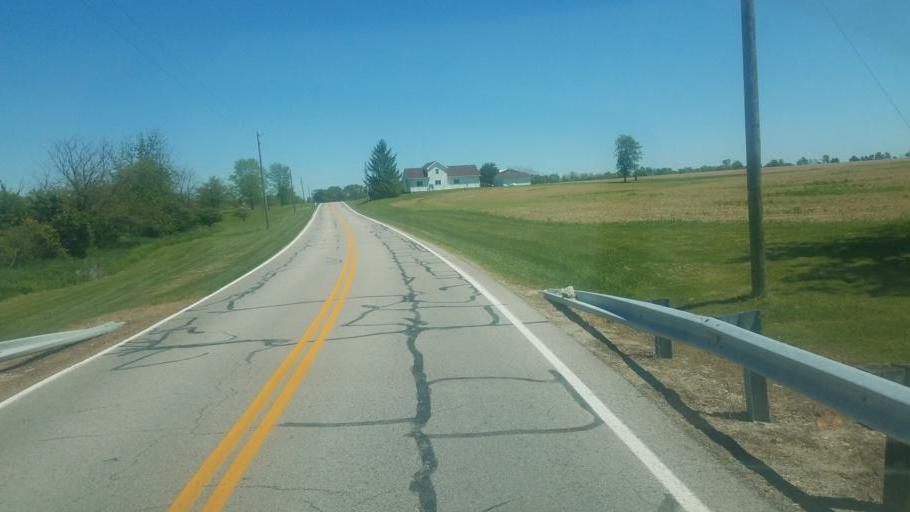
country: US
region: Ohio
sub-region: Miami County
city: Piqua
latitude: 40.2105
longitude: -84.2852
